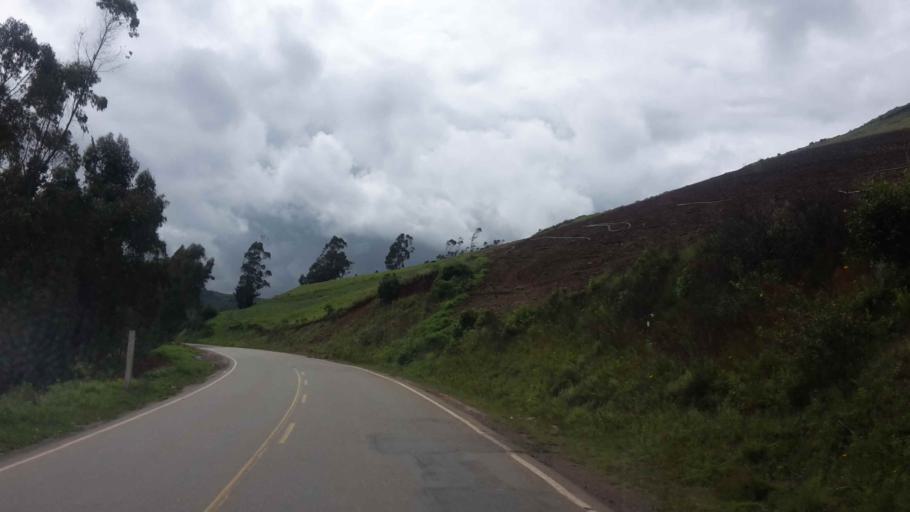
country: BO
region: Cochabamba
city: Totora
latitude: -17.5505
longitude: -65.3524
